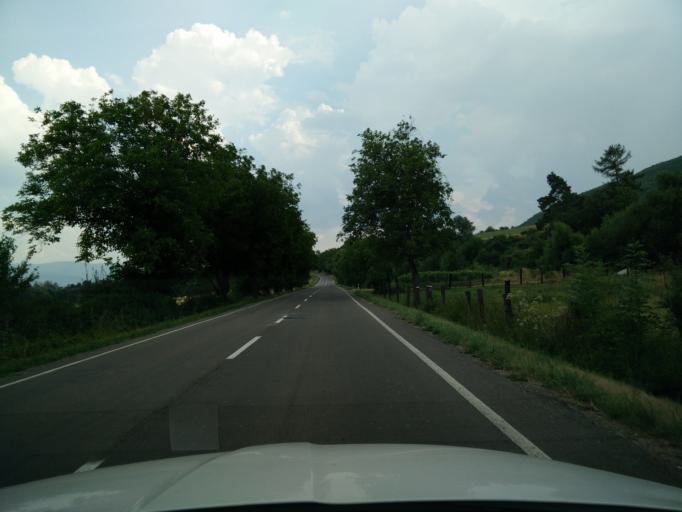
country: SK
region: Nitriansky
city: Novaky
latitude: 48.7732
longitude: 18.4901
